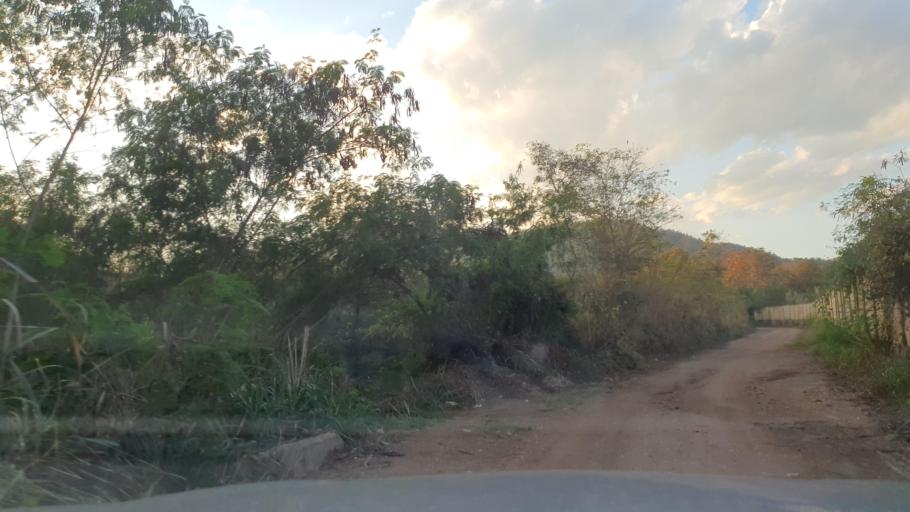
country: TH
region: Chiang Mai
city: Hang Dong
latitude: 18.7349
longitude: 98.8832
